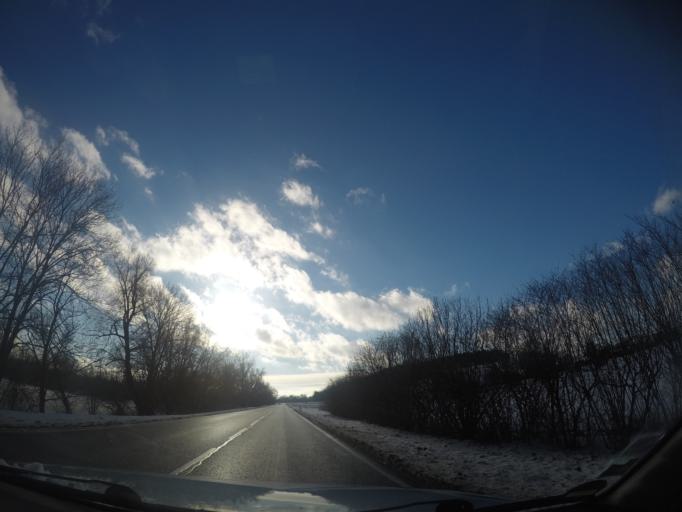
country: DE
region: Baden-Wuerttemberg
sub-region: Tuebingen Region
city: Dettingen
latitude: 48.2466
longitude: 9.7119
